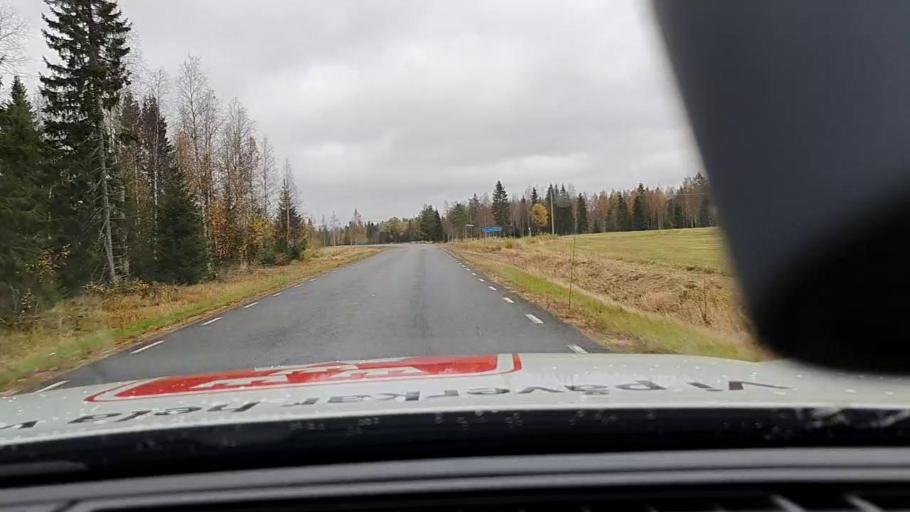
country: SE
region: Norrbotten
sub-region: Haparanda Kommun
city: Haparanda
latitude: 65.9317
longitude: 23.8158
